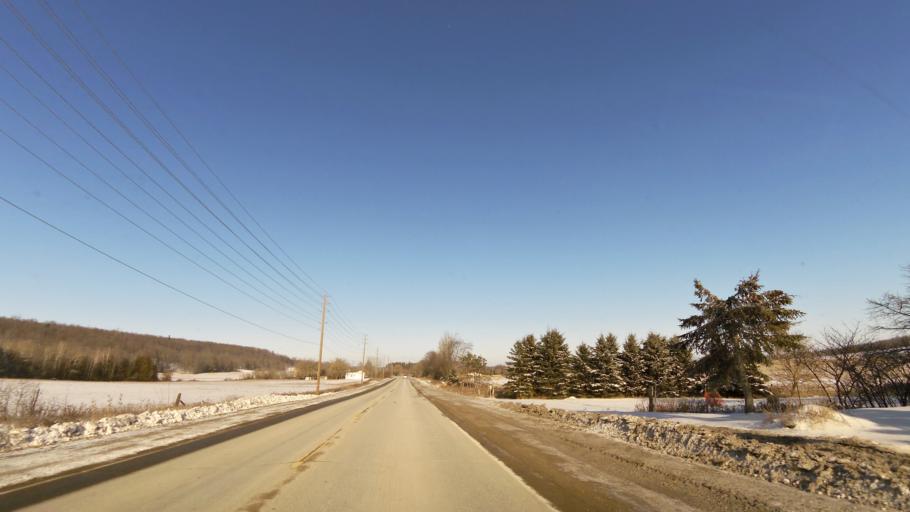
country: CA
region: Ontario
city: Quinte West
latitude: 44.1825
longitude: -77.8099
